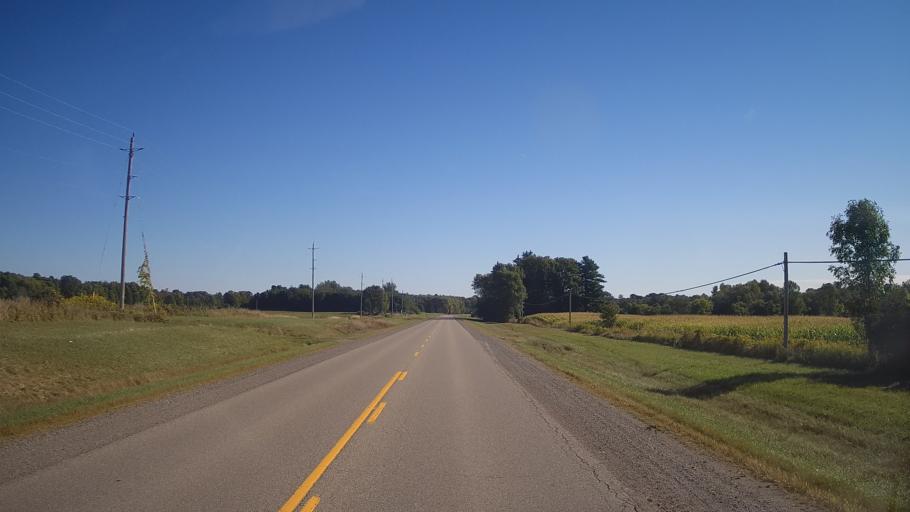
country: CA
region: Ontario
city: Gananoque
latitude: 44.6017
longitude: -76.0787
